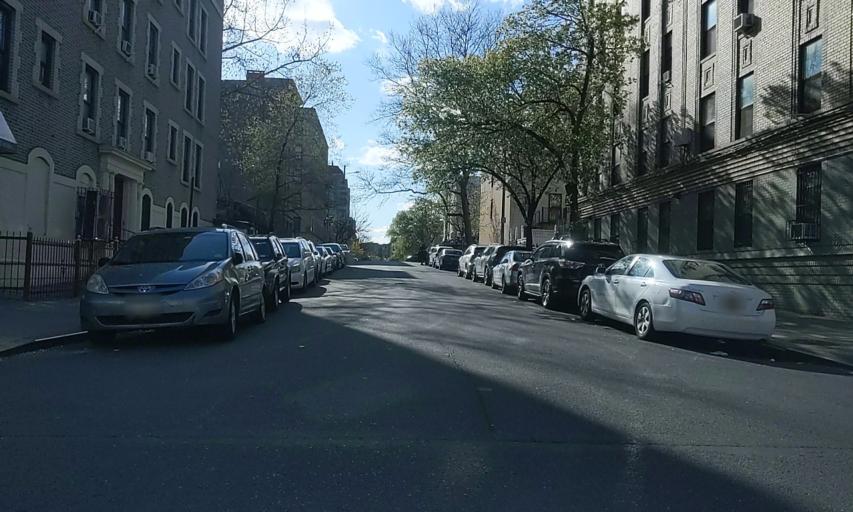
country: US
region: New York
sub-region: New York County
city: Inwood
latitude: 40.8436
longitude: -73.9059
